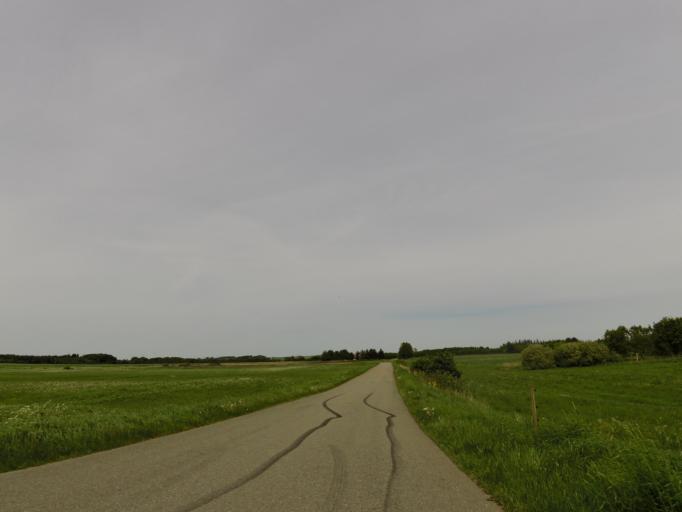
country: DK
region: Central Jutland
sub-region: Holstebro Kommune
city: Vinderup
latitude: 56.5478
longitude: 8.8869
